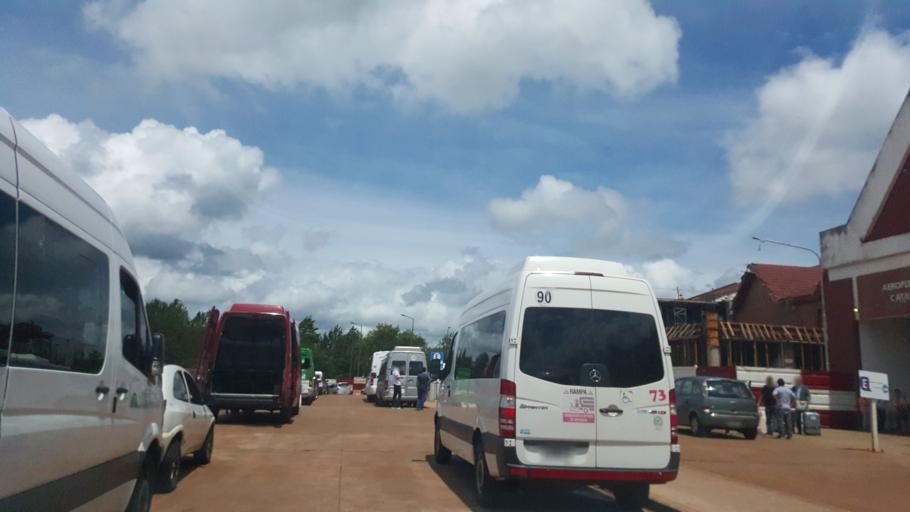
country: AR
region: Misiones
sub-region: Departamento de Iguazu
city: Puerto Iguazu
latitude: -25.7313
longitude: -54.4763
